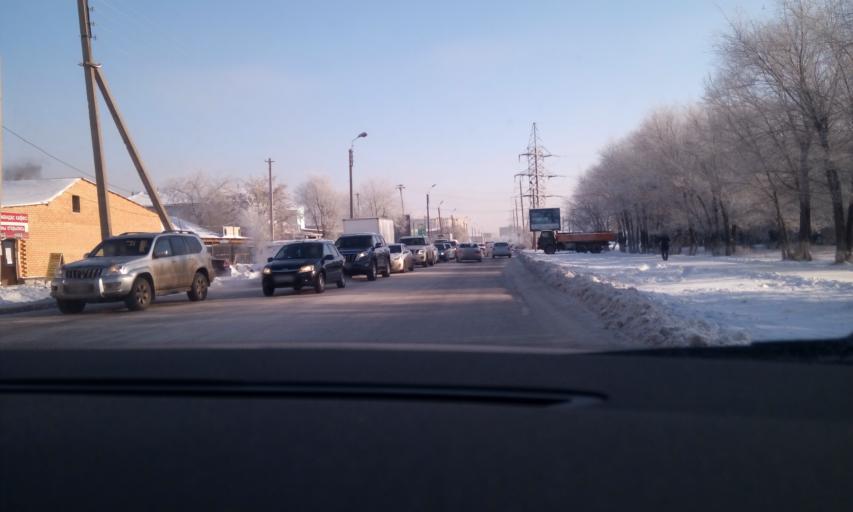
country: KZ
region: Astana Qalasy
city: Astana
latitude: 51.1729
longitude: 71.4384
